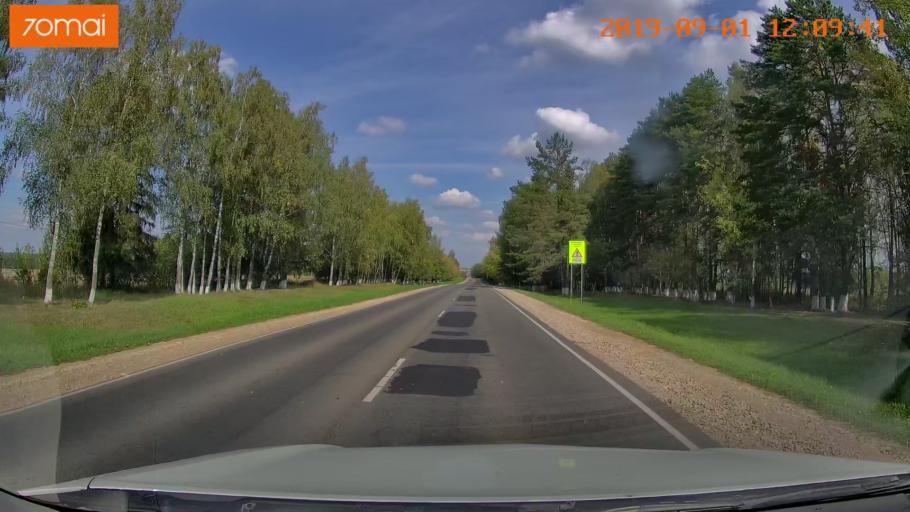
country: RU
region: Kaluga
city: Maloyaroslavets
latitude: 54.9832
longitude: 36.4277
